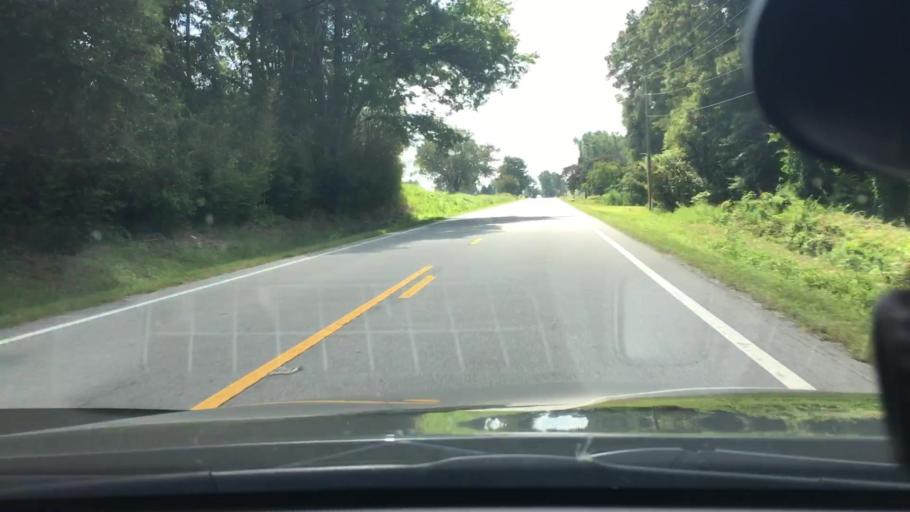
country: US
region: North Carolina
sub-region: Pitt County
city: Farmville
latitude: 35.6856
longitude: -77.4934
